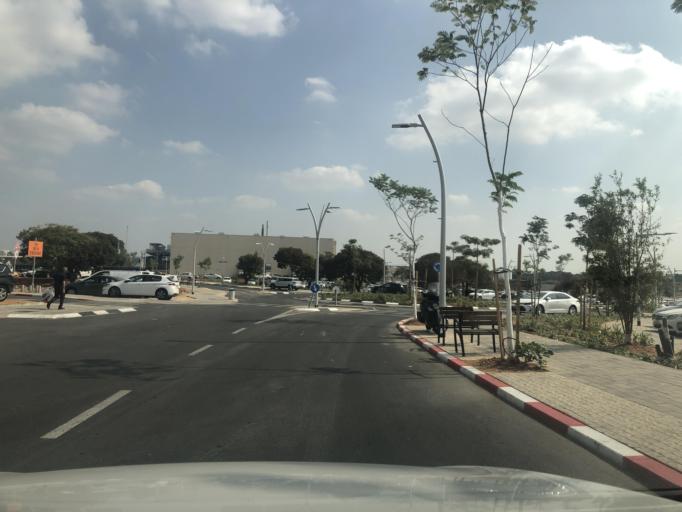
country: IL
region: Tel Aviv
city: Or Yehuda
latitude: 32.0443
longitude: 34.8422
